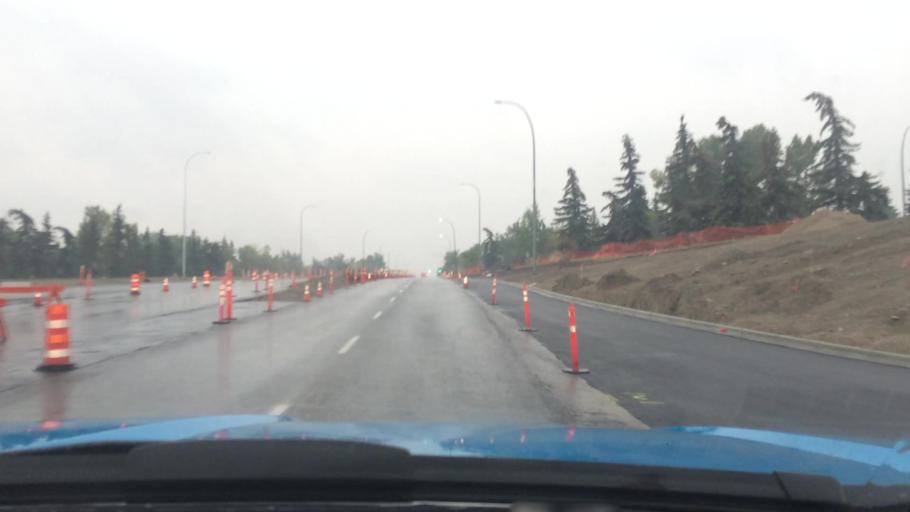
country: CA
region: Alberta
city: Calgary
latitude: 51.0956
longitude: -113.9586
